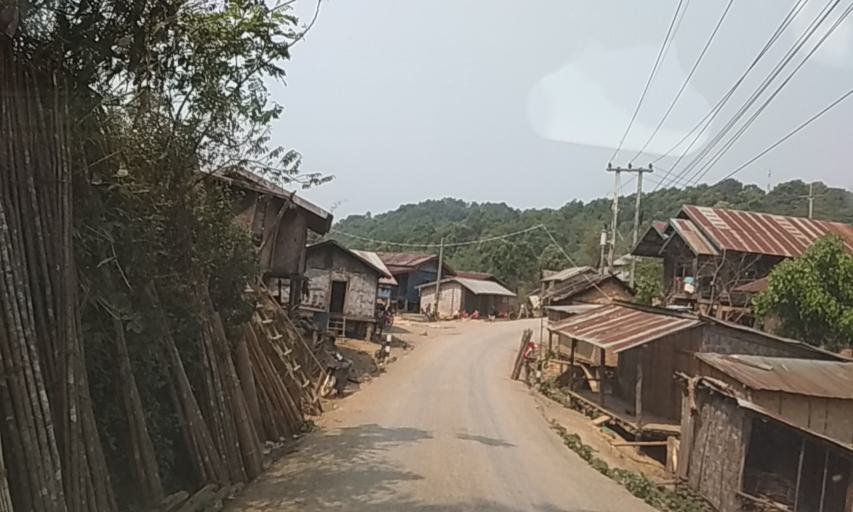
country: TH
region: Nan
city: Chaloem Phra Kiat
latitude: 20.0152
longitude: 101.1158
